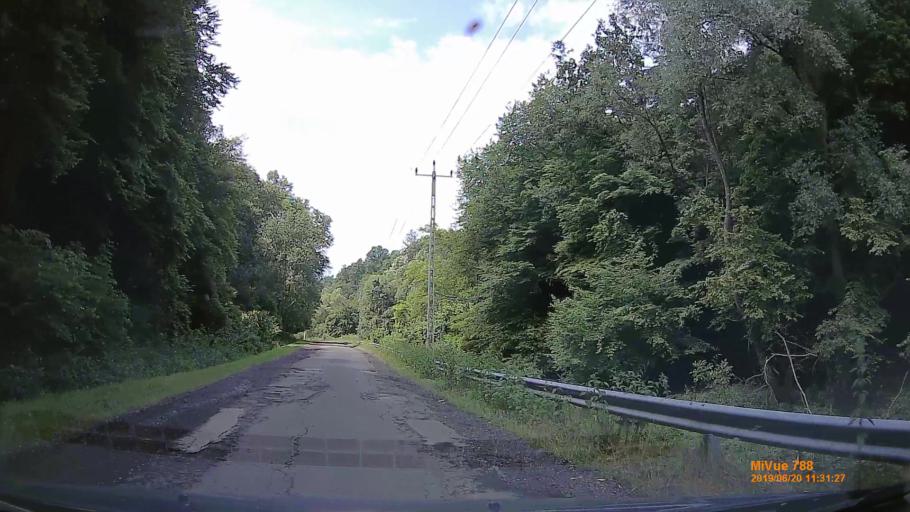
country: HU
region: Baranya
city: Mecseknadasd
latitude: 46.2240
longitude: 18.4303
